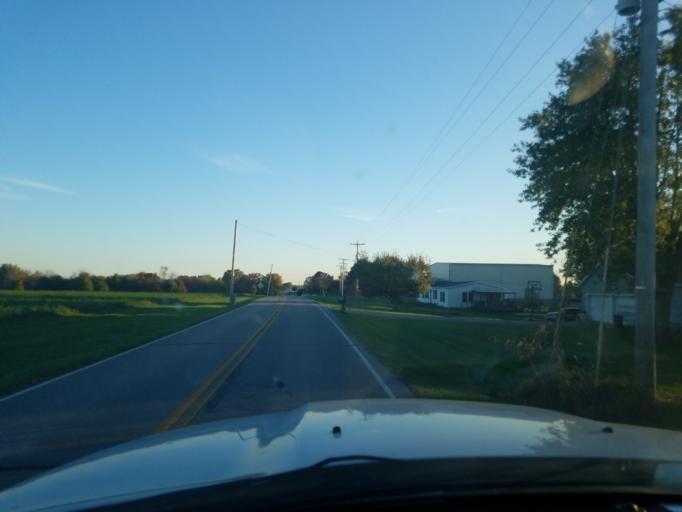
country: US
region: Indiana
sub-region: Floyd County
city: Galena
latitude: 38.3877
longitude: -85.9063
